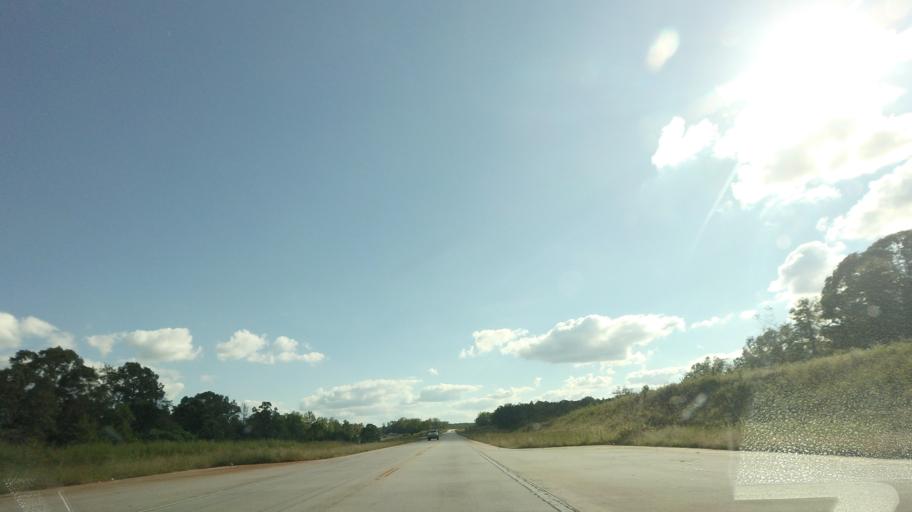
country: US
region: Georgia
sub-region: Lamar County
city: Barnesville
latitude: 33.0493
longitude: -84.1291
